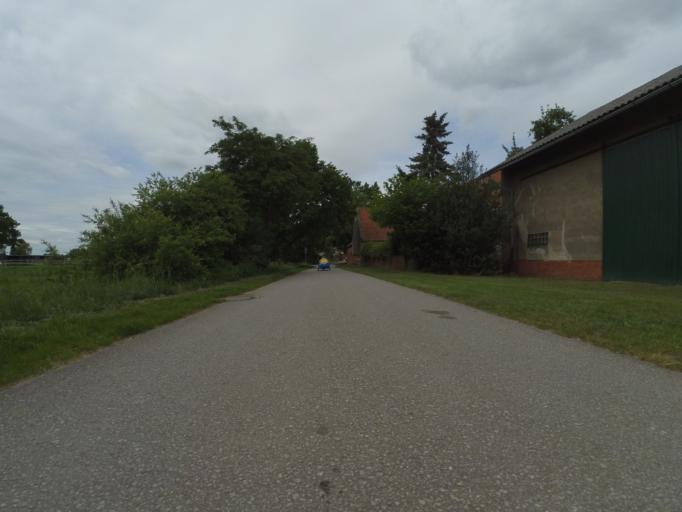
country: DE
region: Lower Saxony
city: Wunstorf
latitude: 52.4543
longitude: 9.3998
